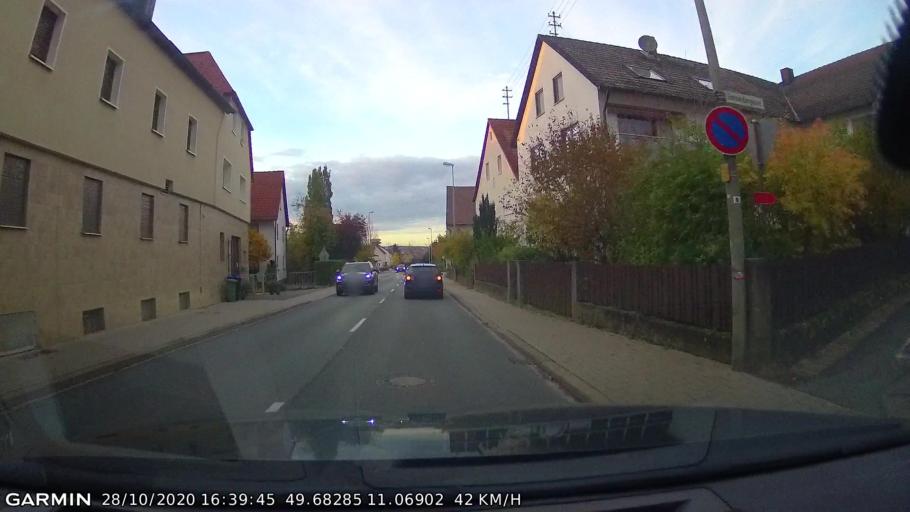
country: DE
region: Bavaria
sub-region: Upper Franconia
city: Poxdorf
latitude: 49.6829
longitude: 11.0690
